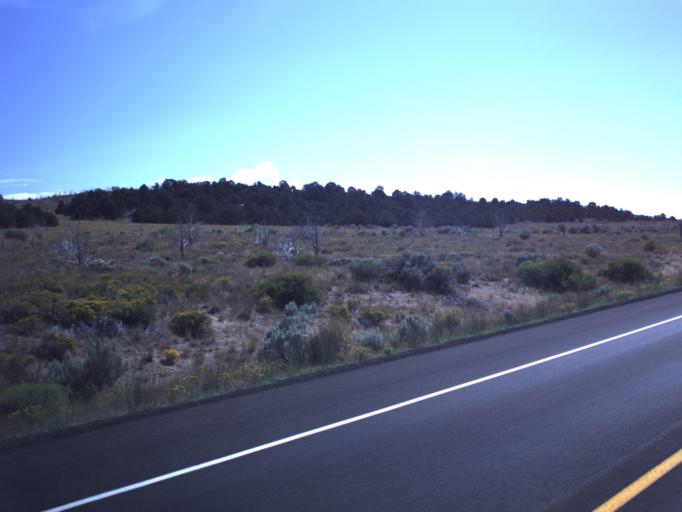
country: US
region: Utah
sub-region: Utah County
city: Genola
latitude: 39.9600
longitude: -112.2462
